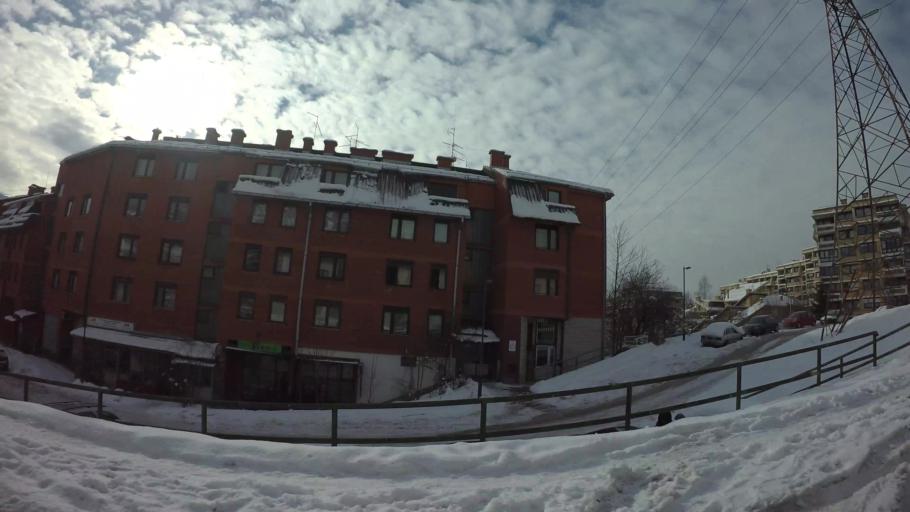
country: BA
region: Federation of Bosnia and Herzegovina
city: Kobilja Glava
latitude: 43.8718
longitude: 18.4210
